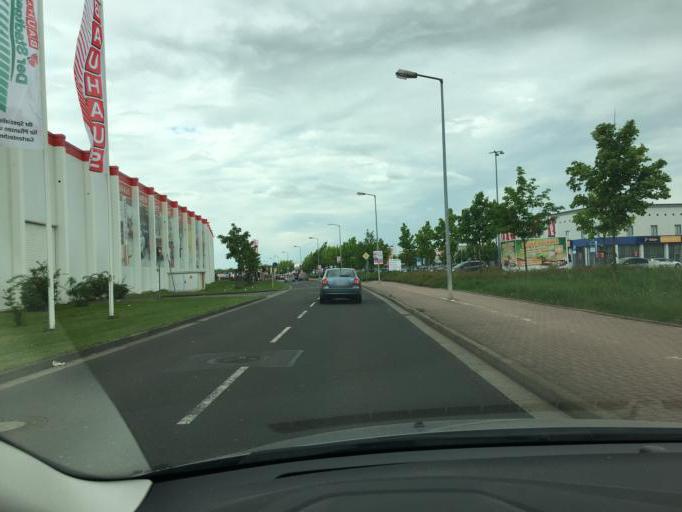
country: DE
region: Saxony
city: Rackwitz
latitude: 51.4003
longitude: 12.4005
